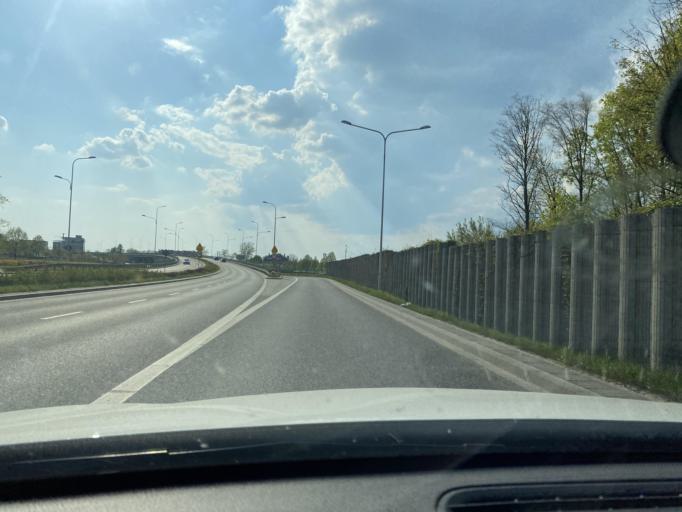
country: PL
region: Lower Silesian Voivodeship
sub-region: Powiat trzebnicki
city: Psary
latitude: 51.1578
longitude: 17.0167
